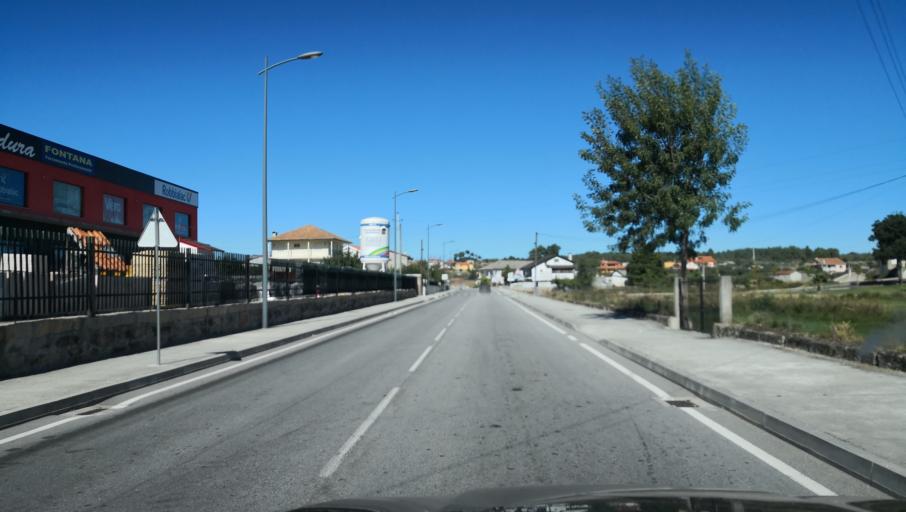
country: PT
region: Vila Real
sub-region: Valpacos
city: Valpacos
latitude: 41.5936
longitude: -7.3064
